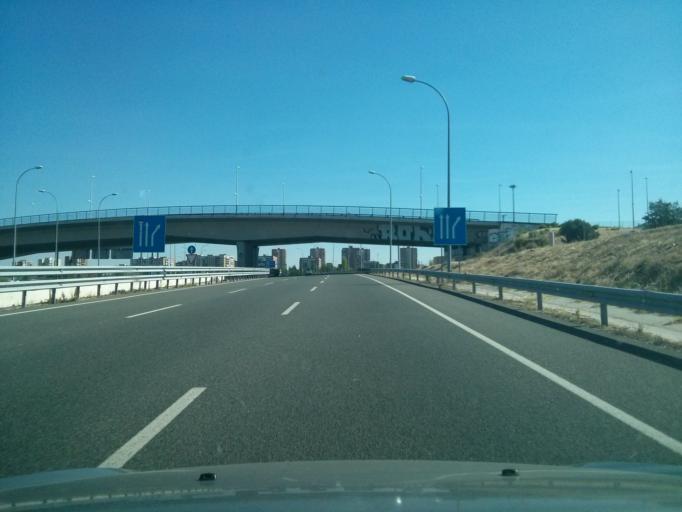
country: ES
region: Madrid
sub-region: Provincia de Madrid
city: Hortaleza
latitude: 40.4860
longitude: -3.6447
